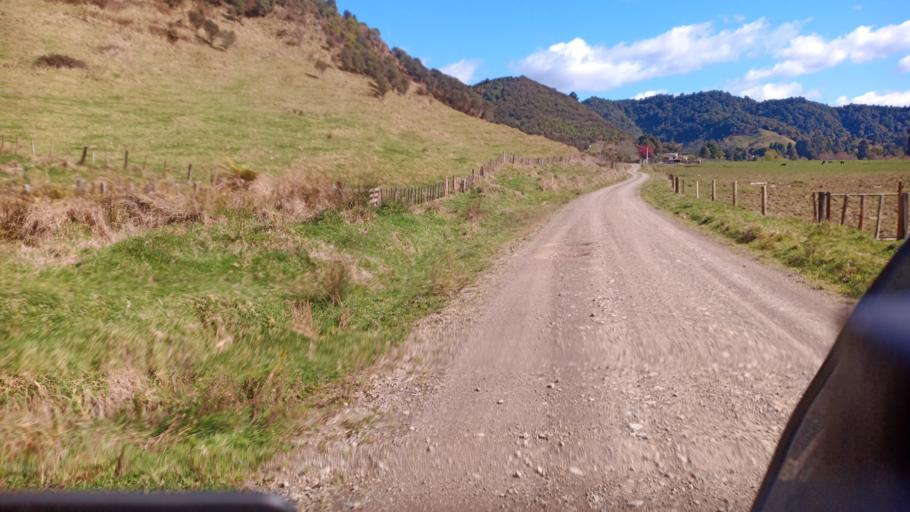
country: NZ
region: Bay of Plenty
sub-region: Opotiki District
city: Opotiki
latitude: -38.1105
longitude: 177.5215
